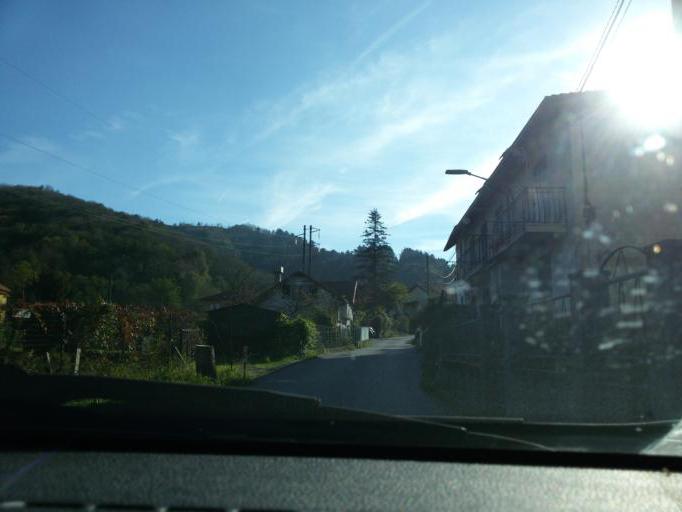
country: IT
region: Liguria
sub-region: Provincia di Genova
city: Davagna
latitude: 44.4838
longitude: 9.1216
